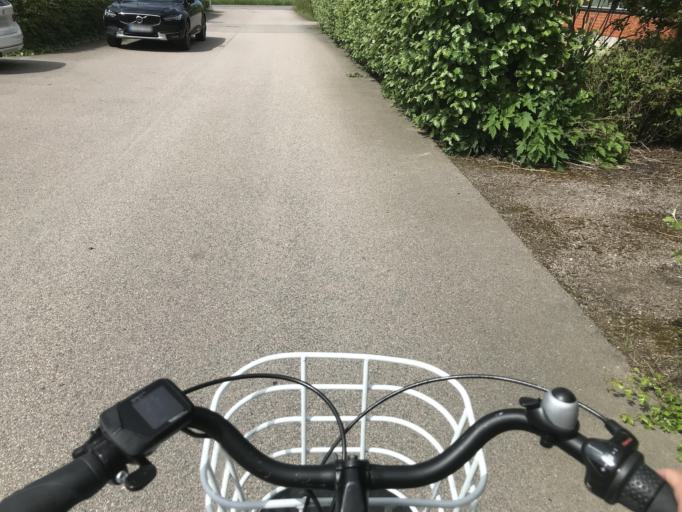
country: SE
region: Skane
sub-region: Landskrona
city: Landskrona
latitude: 55.8976
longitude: 12.8611
